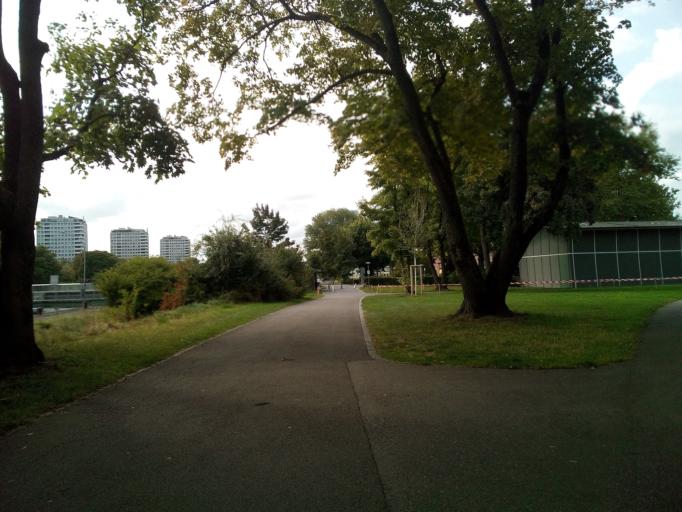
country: CH
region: Basel-Landschaft
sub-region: Bezirk Arlesheim
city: Birsfelden
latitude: 47.5593
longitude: 7.6294
